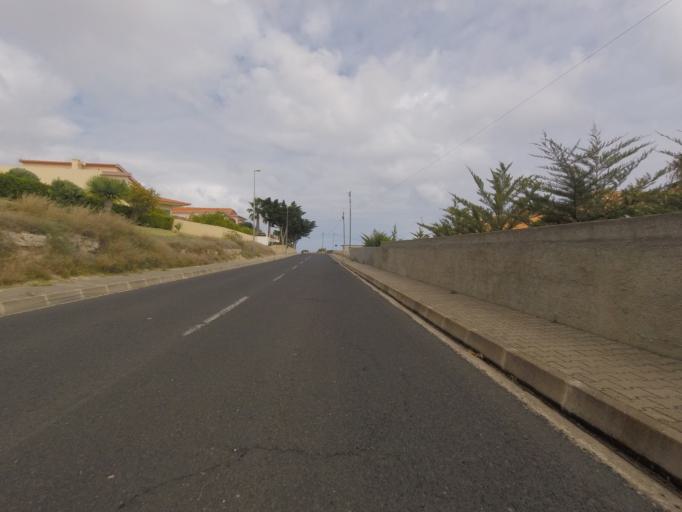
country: PT
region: Madeira
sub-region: Porto Santo
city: Vila de Porto Santo
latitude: 33.0541
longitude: -16.3465
